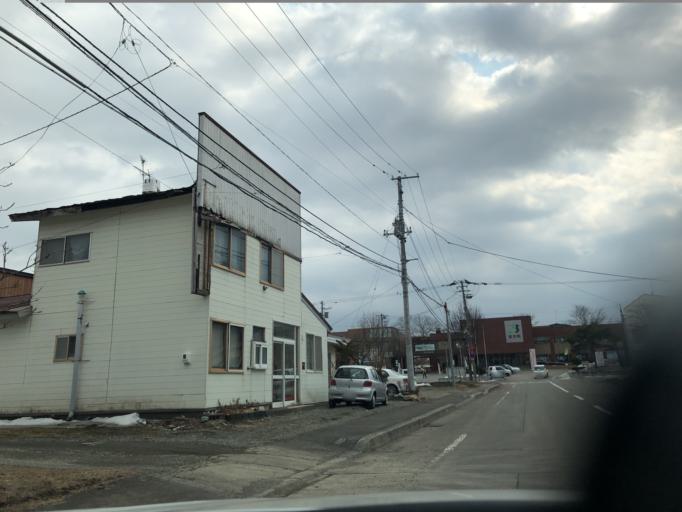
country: JP
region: Hokkaido
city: Chitose
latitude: 42.7636
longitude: 141.8169
